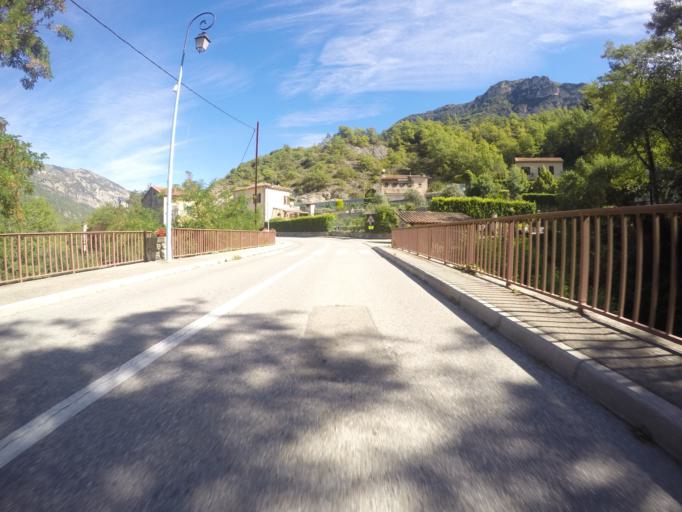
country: FR
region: Provence-Alpes-Cote d'Azur
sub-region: Departement des Alpes-Maritimes
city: Gilette
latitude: 43.9629
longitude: 7.1537
